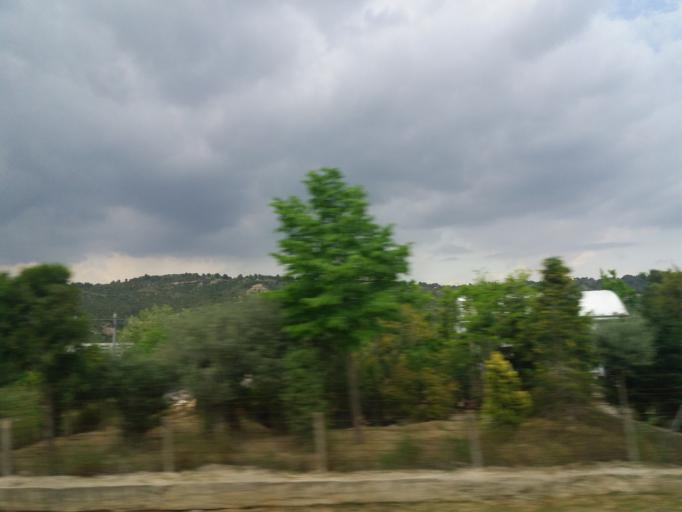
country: ES
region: Catalonia
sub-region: Provincia de Barcelona
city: Abrera
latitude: 41.5313
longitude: 1.9042
